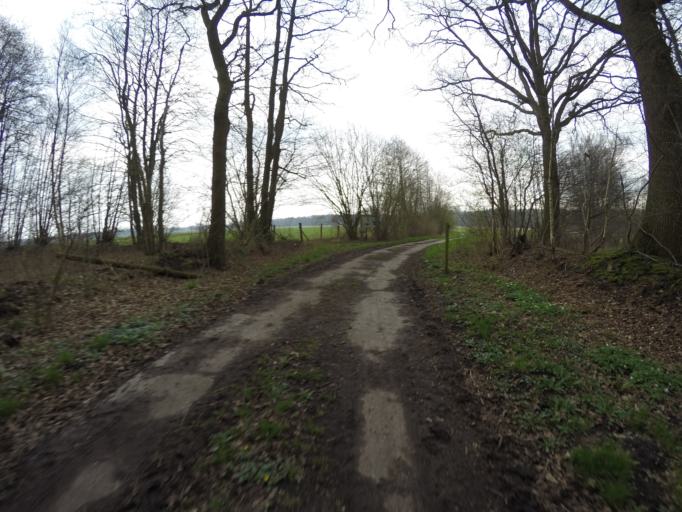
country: DE
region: Schleswig-Holstein
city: Ellerhoop
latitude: 53.7279
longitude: 9.8086
